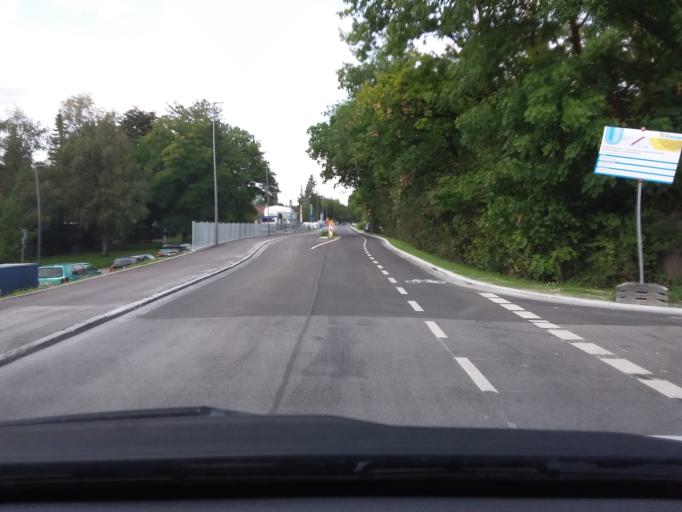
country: DE
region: Bavaria
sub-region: Upper Bavaria
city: Unterschleissheim
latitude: 48.2811
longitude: 11.5872
